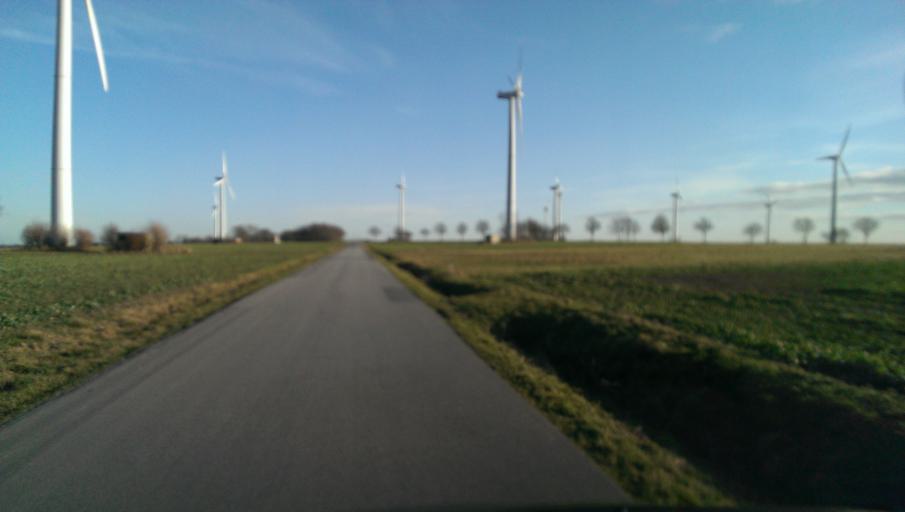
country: DE
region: North Rhine-Westphalia
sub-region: Regierungsbezirk Arnsberg
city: Ruthen
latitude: 51.5183
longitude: 8.4360
